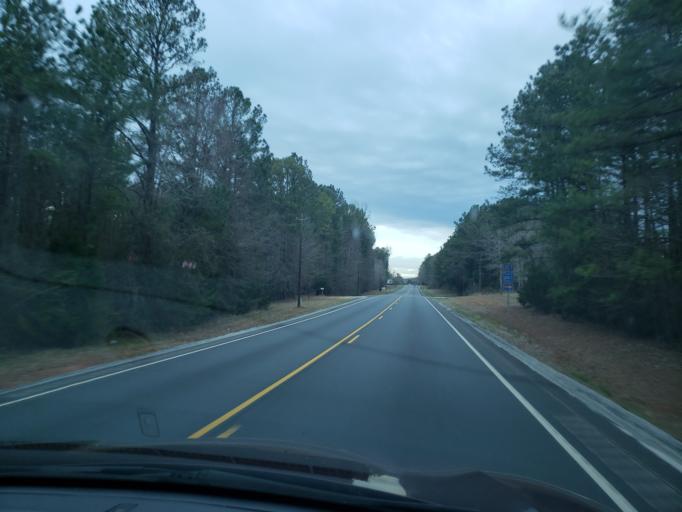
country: US
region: Alabama
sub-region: Randolph County
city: Roanoke
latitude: 33.0323
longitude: -85.3473
